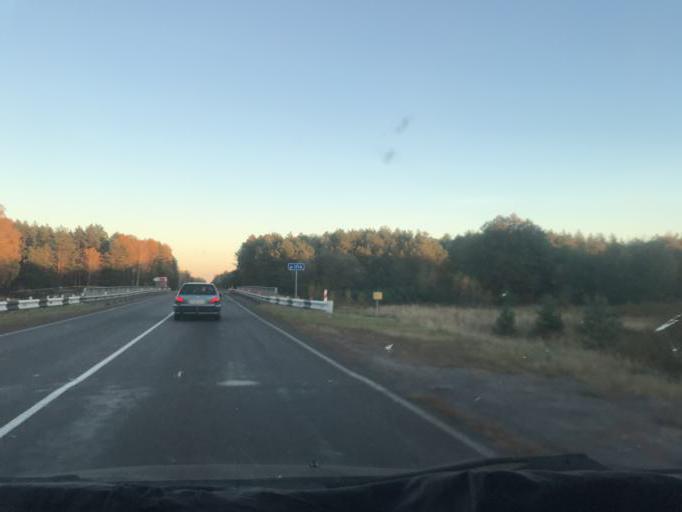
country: BY
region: Gomel
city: Mazyr
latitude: 52.2006
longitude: 29.0860
